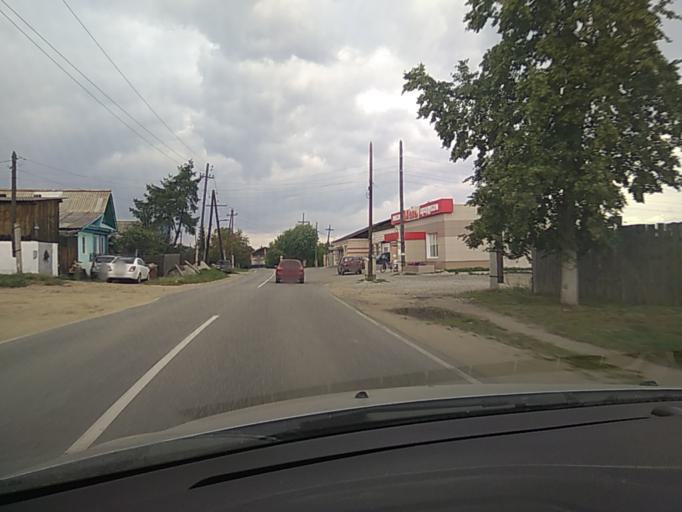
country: RU
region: Chelyabinsk
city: Kyshtym
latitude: 55.7111
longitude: 60.5132
